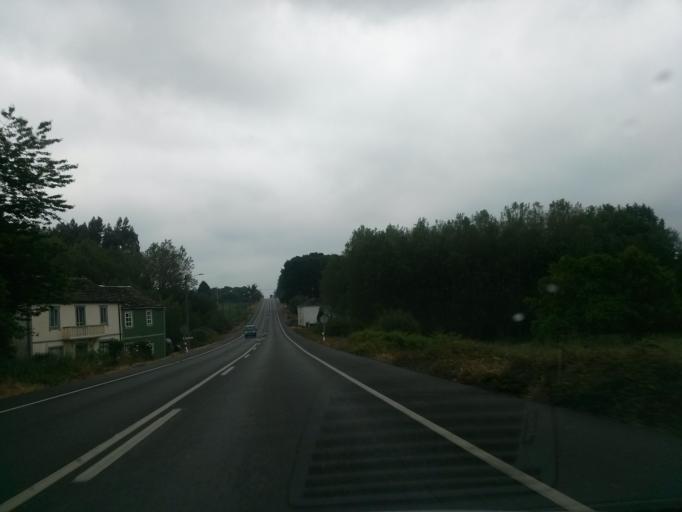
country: ES
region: Galicia
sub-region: Provincia de Lugo
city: Begonte
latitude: 43.1355
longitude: -7.6592
